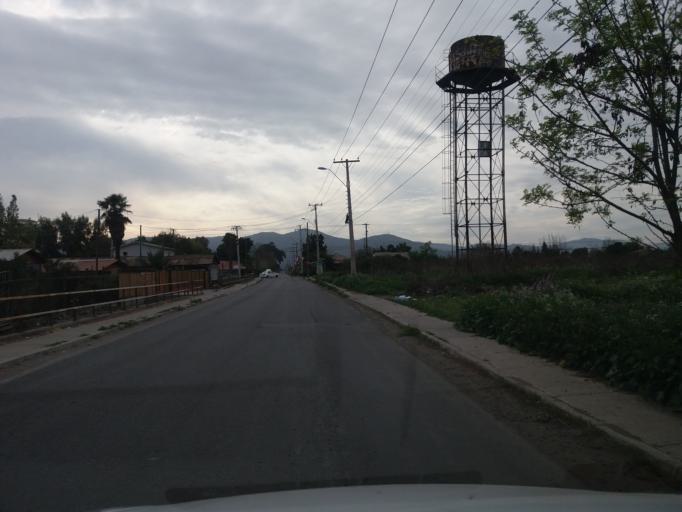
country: CL
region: Valparaiso
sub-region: Provincia de Quillota
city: Hacienda La Calera
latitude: -32.7880
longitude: -71.1716
